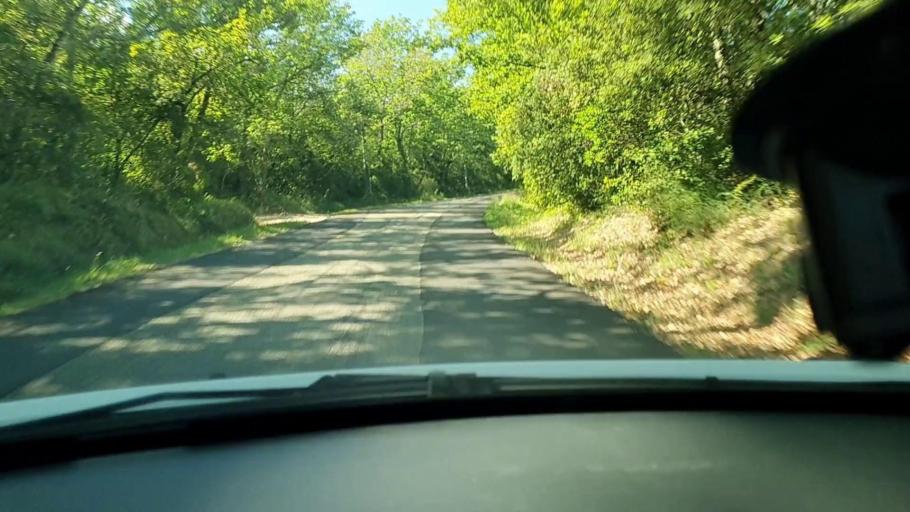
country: FR
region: Languedoc-Roussillon
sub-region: Departement du Gard
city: Sabran
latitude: 44.1749
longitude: 4.5109
